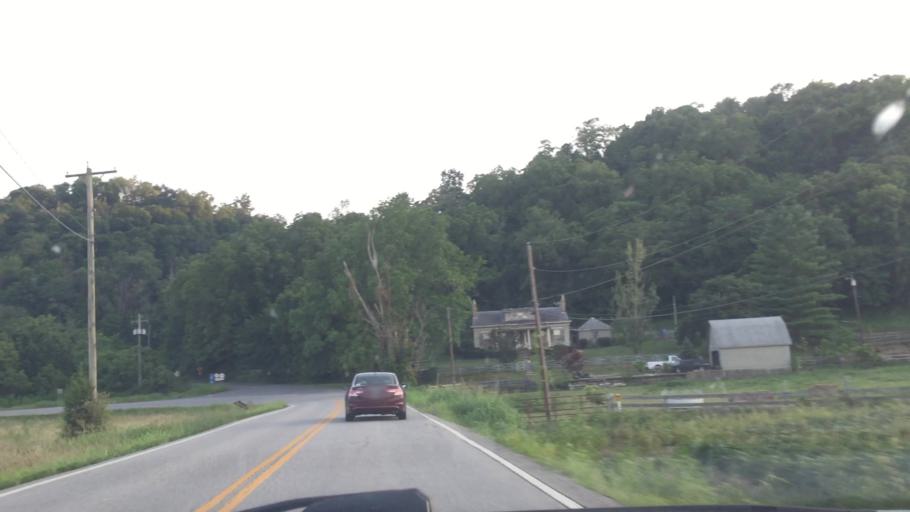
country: US
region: Kentucky
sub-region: Carroll County
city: Carrollton
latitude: 38.6753
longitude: -85.1957
